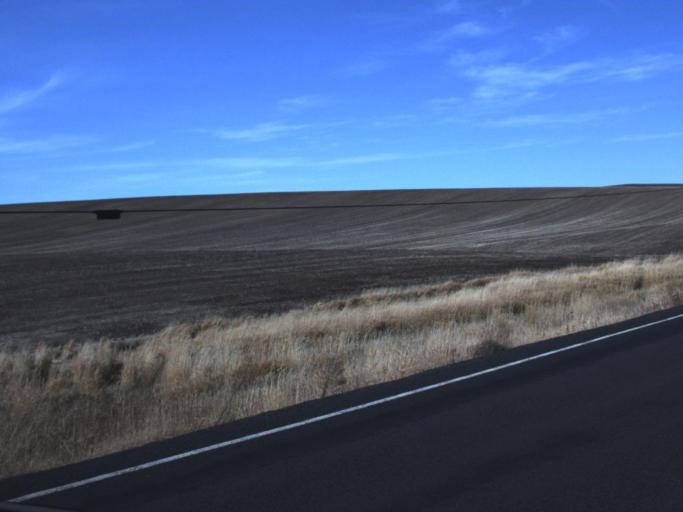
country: US
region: Washington
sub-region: Lincoln County
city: Davenport
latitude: 47.6897
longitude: -118.1410
